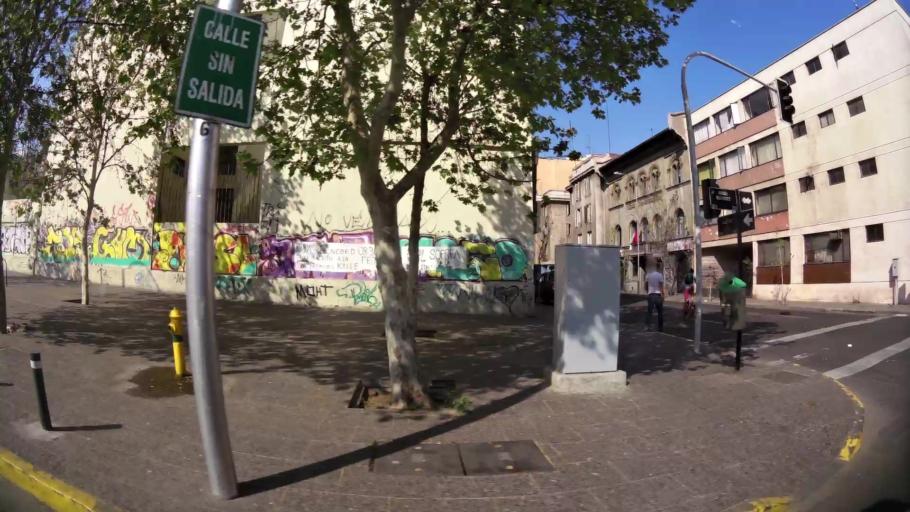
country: CL
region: Santiago Metropolitan
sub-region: Provincia de Santiago
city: Santiago
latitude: -33.4415
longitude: -70.6591
